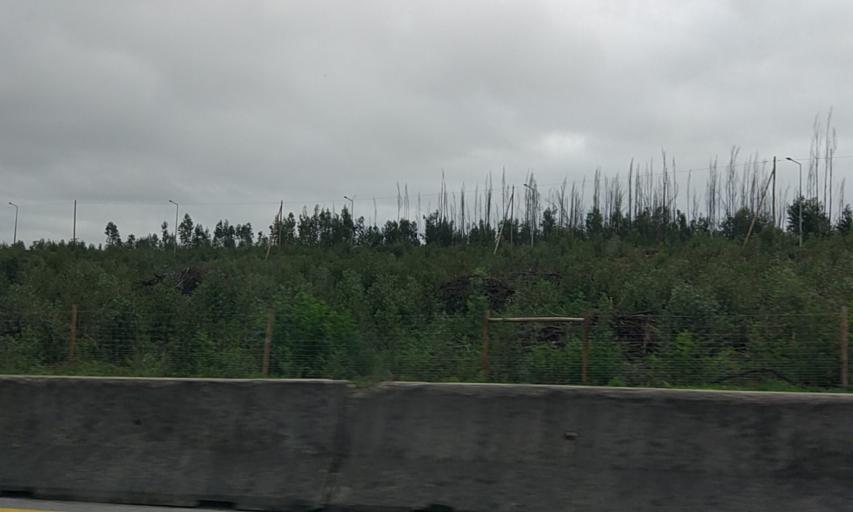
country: PT
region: Viseu
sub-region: Mortagua
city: Mortagua
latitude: 40.3533
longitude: -8.1921
